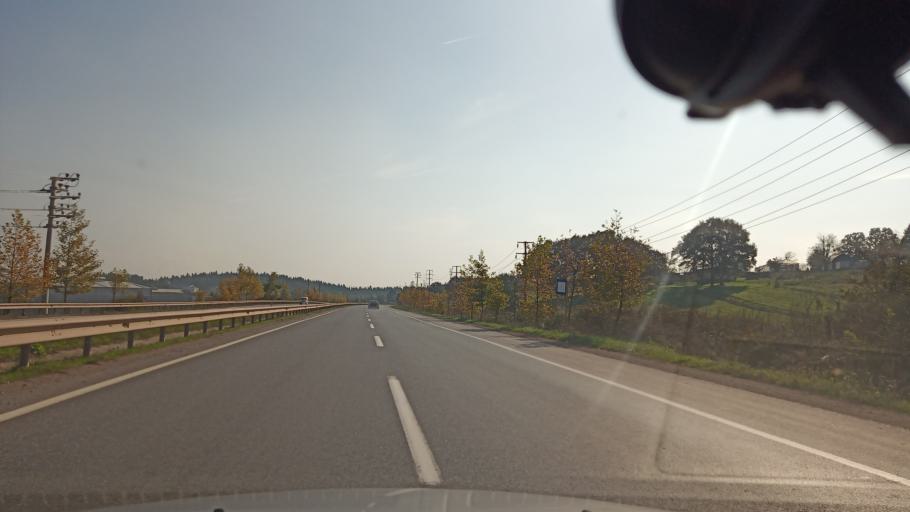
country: TR
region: Sakarya
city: Adapazari
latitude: 40.8327
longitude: 30.3762
